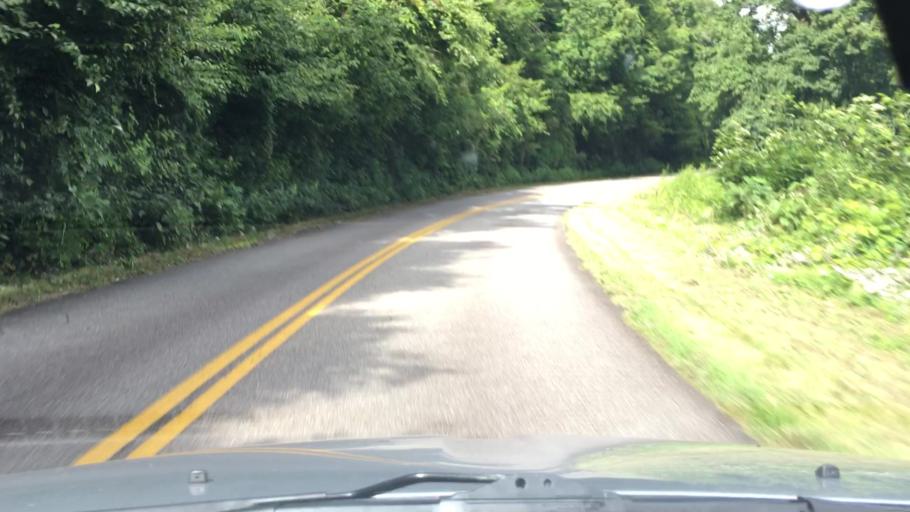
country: US
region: North Carolina
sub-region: McDowell County
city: West Marion
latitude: 35.7518
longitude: -82.1846
